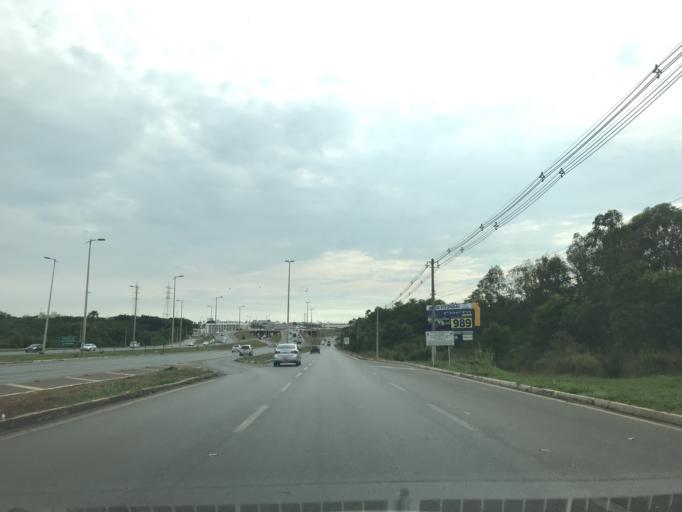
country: BR
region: Federal District
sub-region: Brasilia
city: Brasilia
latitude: -15.8096
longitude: -47.9734
